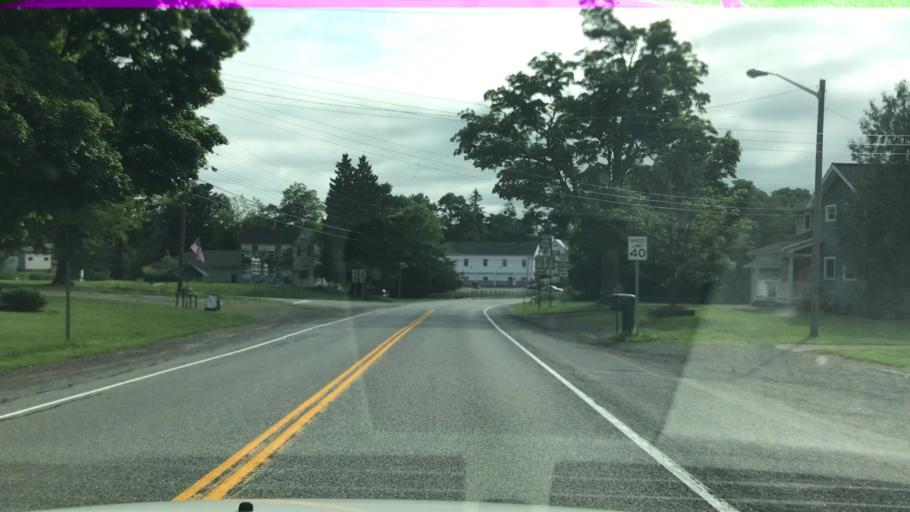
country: US
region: New York
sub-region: Erie County
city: Alden
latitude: 42.8368
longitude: -78.3999
